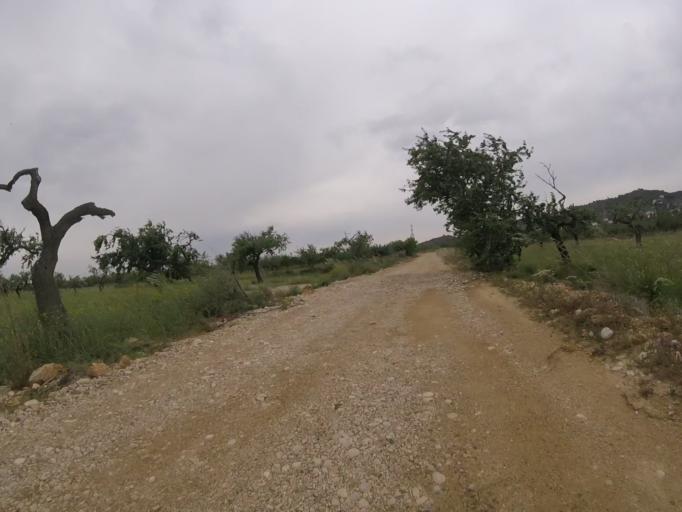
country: ES
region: Valencia
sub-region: Provincia de Castello
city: Alcoceber
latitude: 40.2424
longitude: 0.2635
